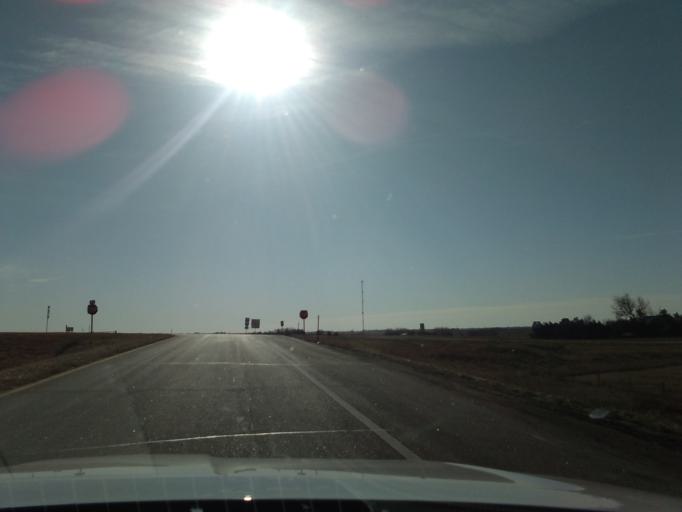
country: US
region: Nebraska
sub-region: Seward County
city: Milford
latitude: 40.8203
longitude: -97.0455
